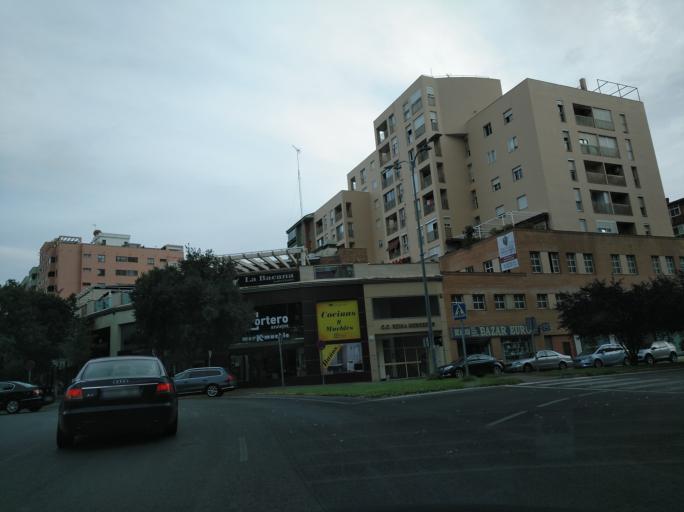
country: ES
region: Extremadura
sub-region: Provincia de Badajoz
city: Badajoz
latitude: 38.8669
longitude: -6.9864
